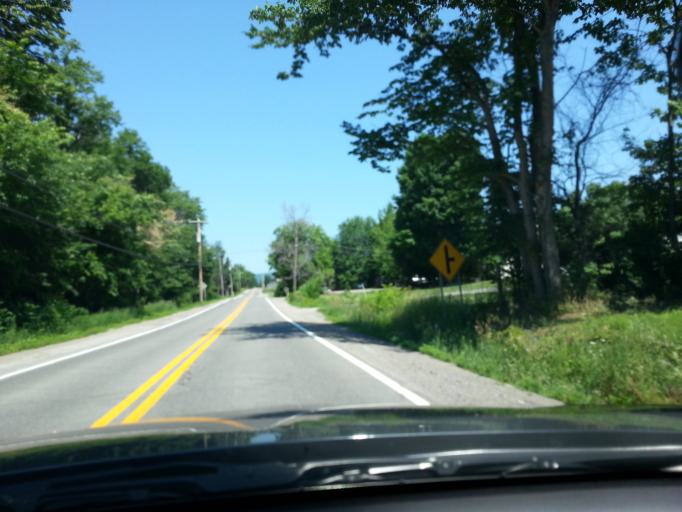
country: CA
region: Ontario
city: Bells Corners
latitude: 45.4441
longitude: -75.9195
